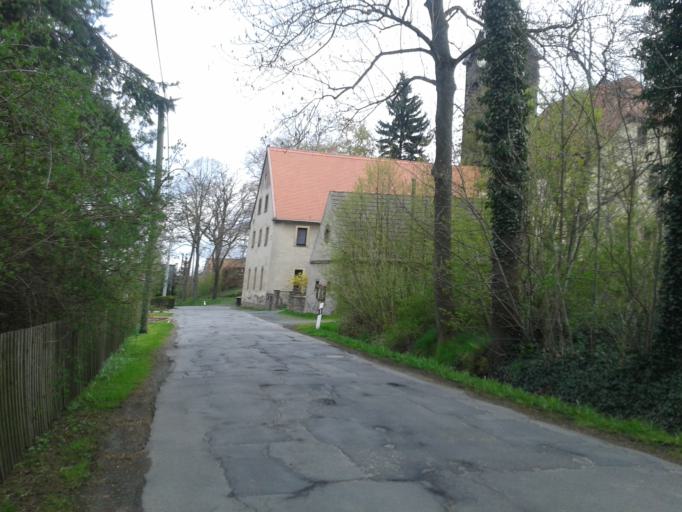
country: DE
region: Saxony
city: Oberschona
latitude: 50.9230
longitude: 13.2999
